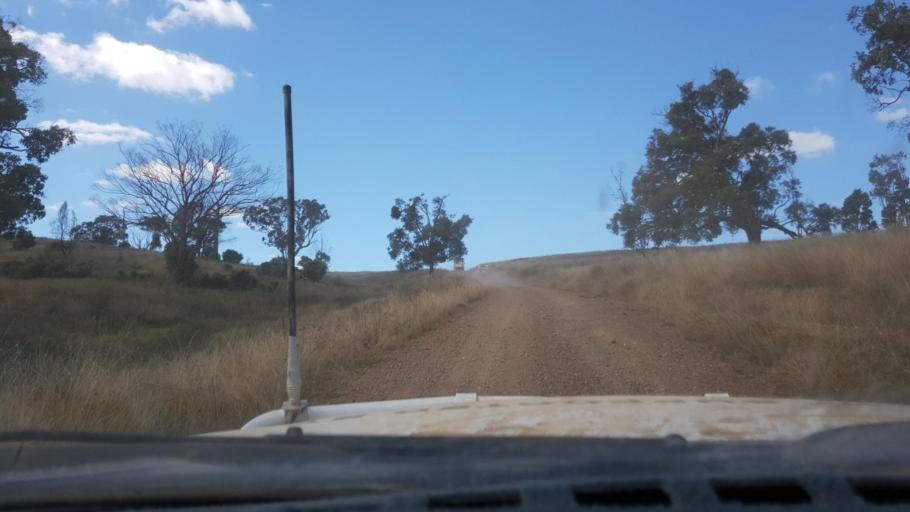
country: AU
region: New South Wales
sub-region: Tamworth Municipality
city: Manilla
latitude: -30.4390
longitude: 150.8480
